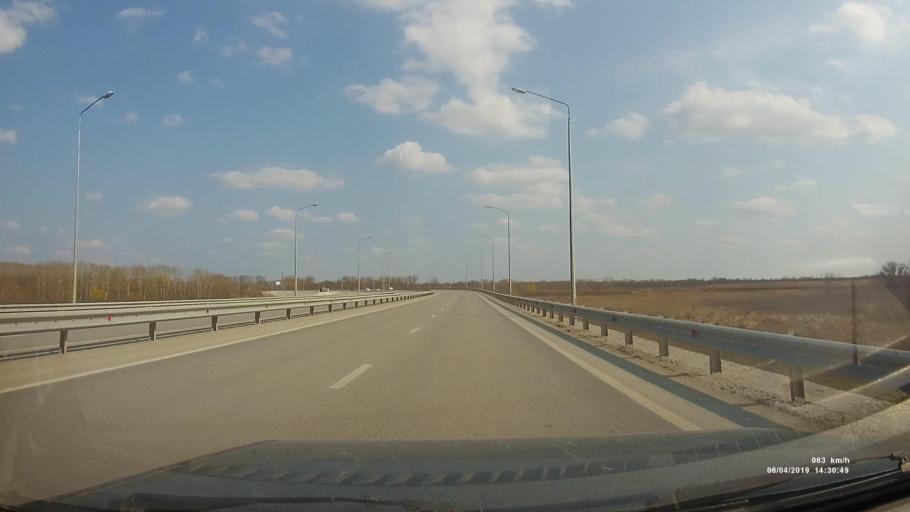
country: RU
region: Rostov
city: Rostov-na-Donu
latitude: 47.2061
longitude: 39.7521
